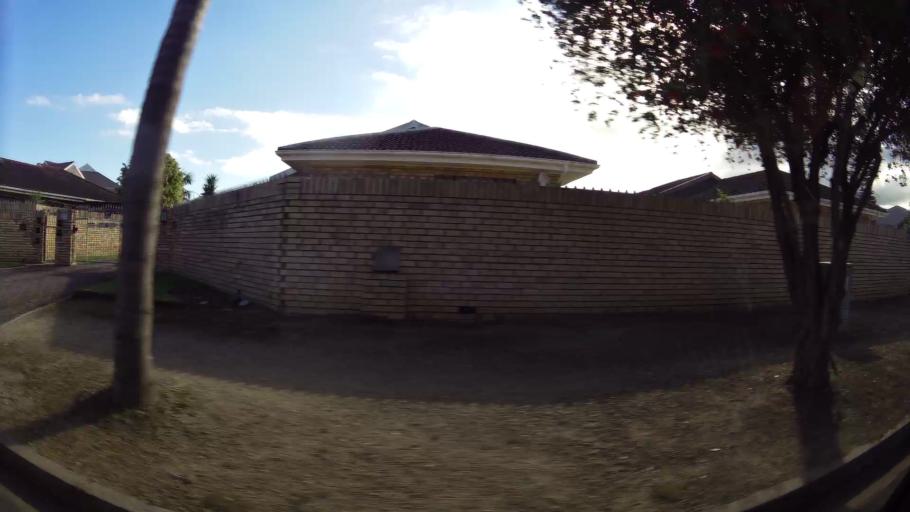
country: ZA
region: Western Cape
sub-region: Eden District Municipality
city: George
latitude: -33.9600
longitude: 22.4893
